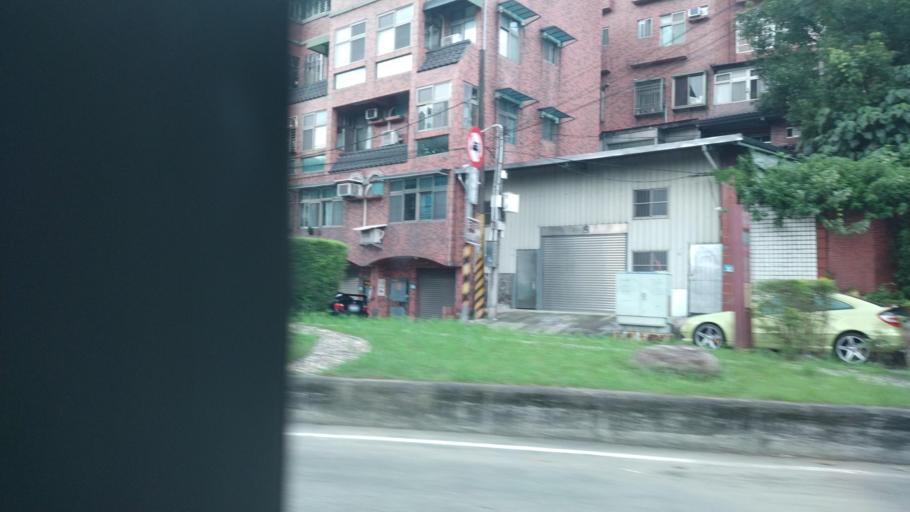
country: TW
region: Taiwan
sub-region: Taoyuan
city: Taoyuan
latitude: 24.9685
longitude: 121.3858
